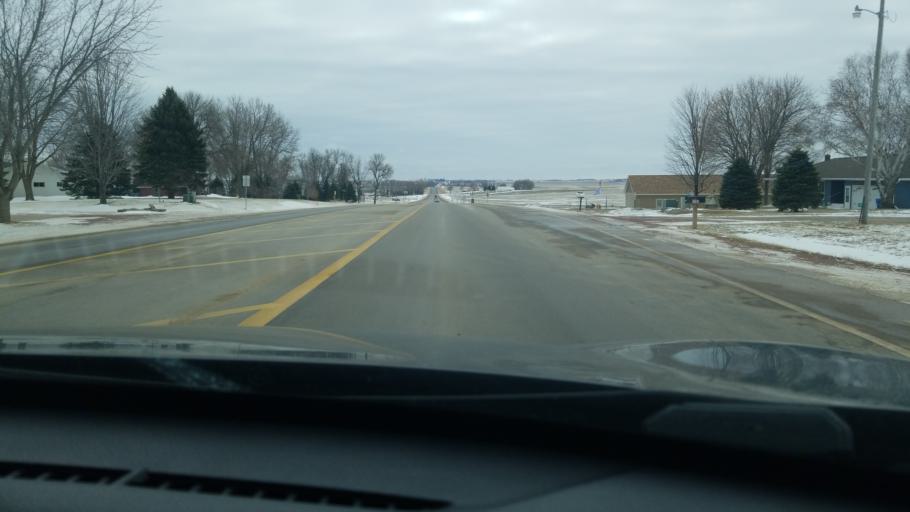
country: US
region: South Dakota
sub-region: Minnehaha County
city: Brandon
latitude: 43.4487
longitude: -96.4296
